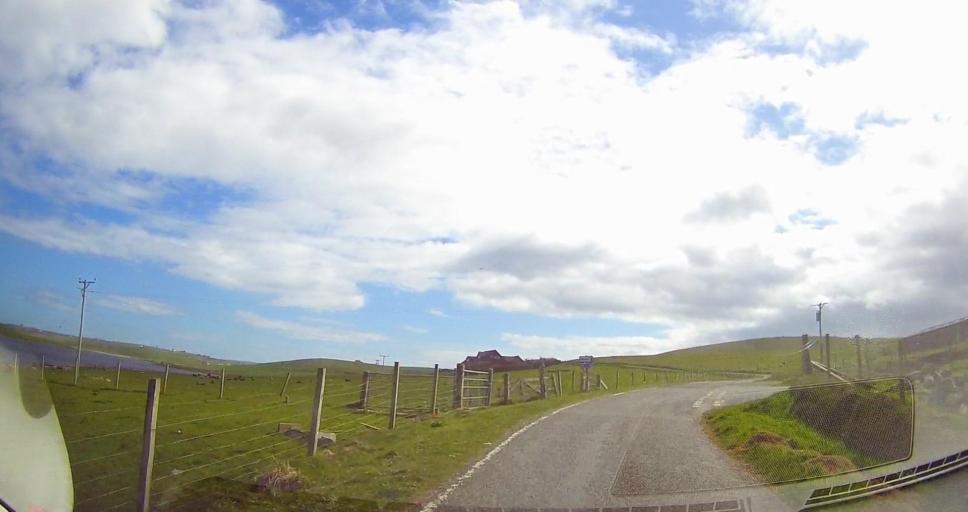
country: GB
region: Scotland
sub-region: Shetland Islands
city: Sandwick
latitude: 59.9334
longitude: -1.3456
